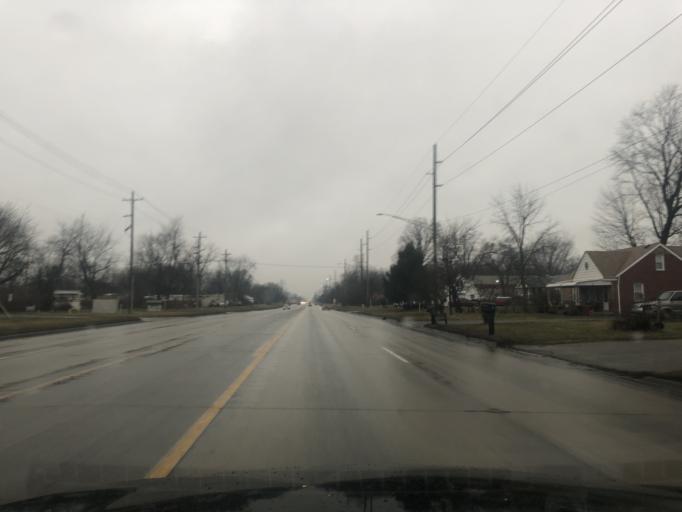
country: US
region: Michigan
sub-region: Wayne County
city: Inkster
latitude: 42.2681
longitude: -83.3173
